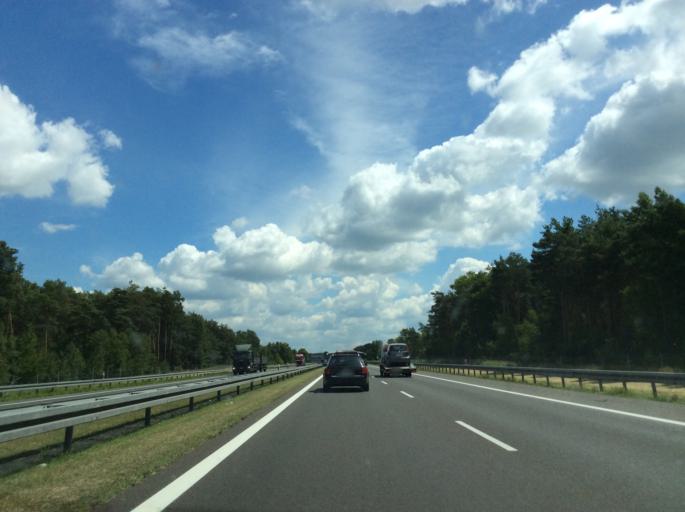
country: PL
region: Greater Poland Voivodeship
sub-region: Powiat koninski
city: Rzgow Pierwszy
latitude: 52.1866
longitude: 18.0875
